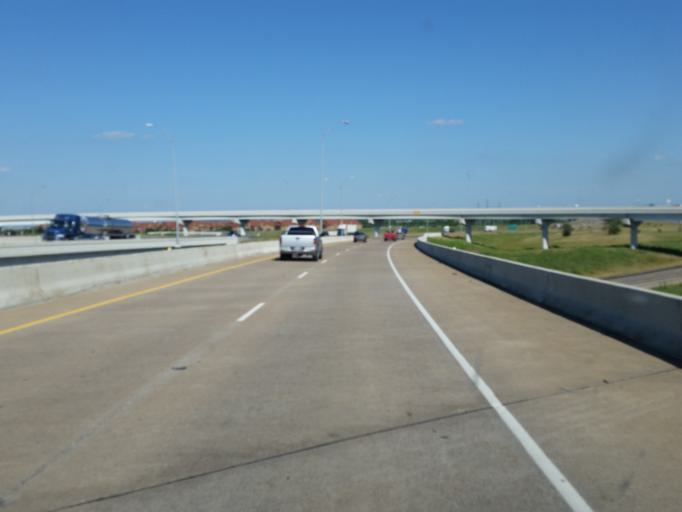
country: US
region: Texas
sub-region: Tarrant County
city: Benbrook
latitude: 32.6945
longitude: -97.4729
